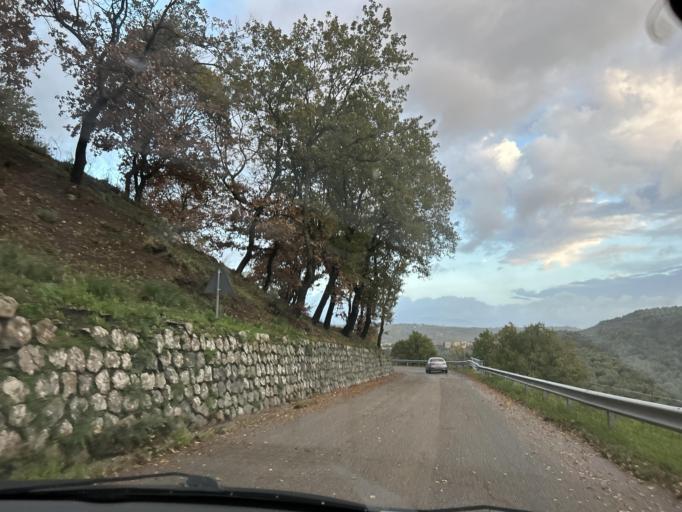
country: IT
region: Calabria
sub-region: Provincia di Catanzaro
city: Squillace
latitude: 38.7679
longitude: 16.5138
